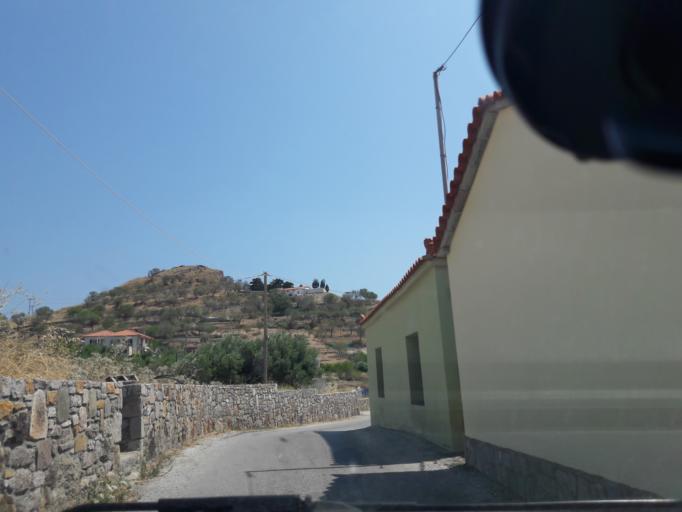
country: GR
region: North Aegean
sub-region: Nomos Lesvou
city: Myrina
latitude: 39.8528
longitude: 25.0871
